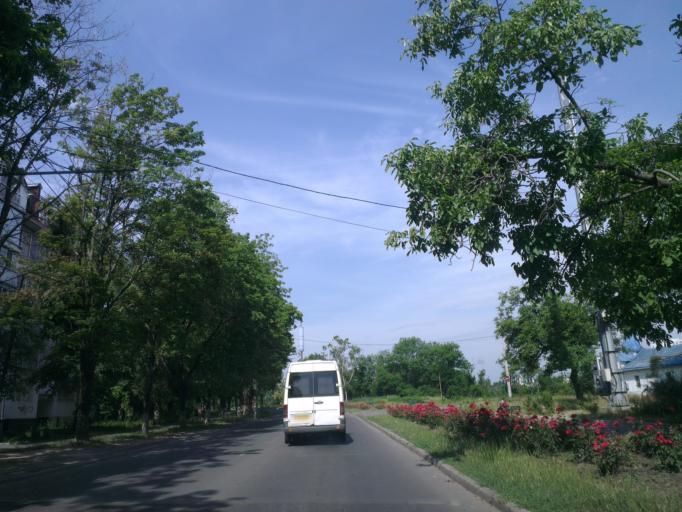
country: MD
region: Chisinau
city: Chisinau
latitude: 46.9989
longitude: 28.8502
